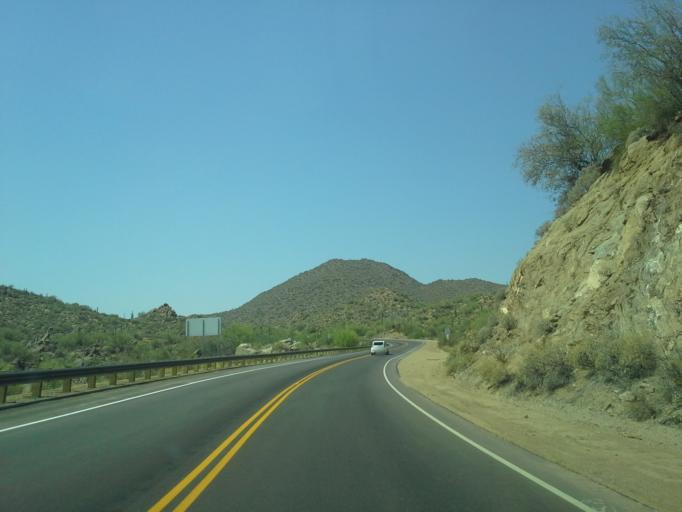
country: US
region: Arizona
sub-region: Pinal County
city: Apache Junction
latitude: 33.5741
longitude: -111.5426
